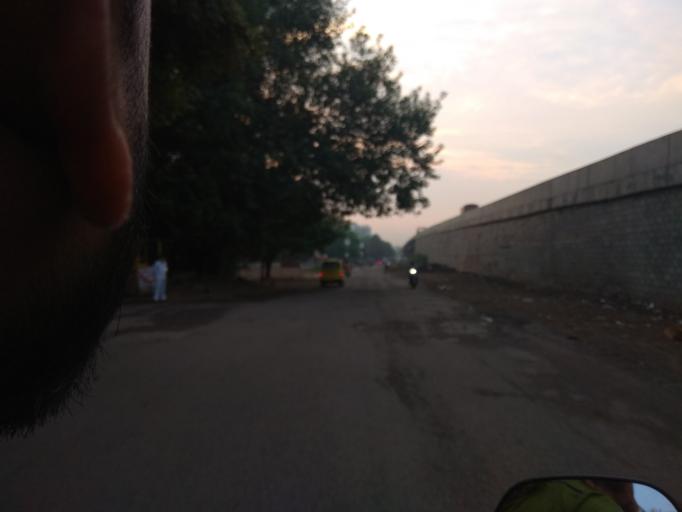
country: IN
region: Maharashtra
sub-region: Pune Division
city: Kharakvasla
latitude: 18.4858
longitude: 73.7982
